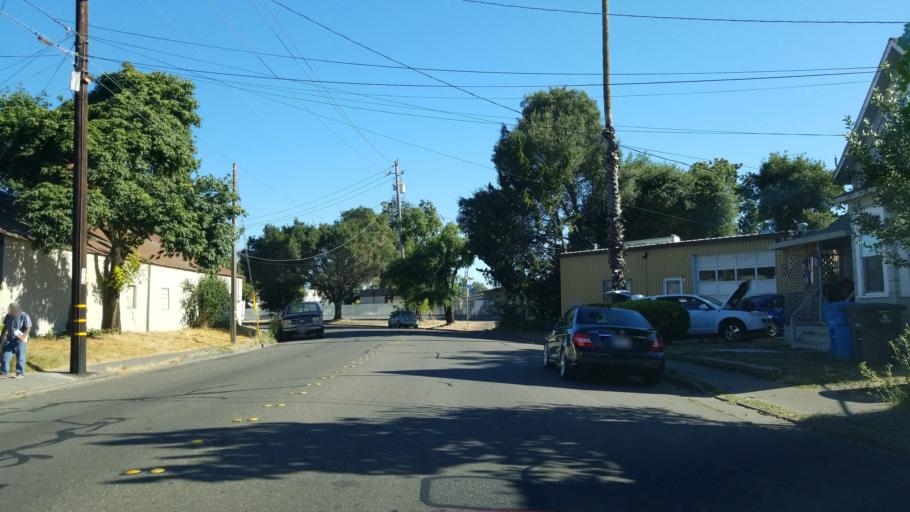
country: US
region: California
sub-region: Sonoma County
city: Santa Rosa
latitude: 38.4448
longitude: -122.7267
